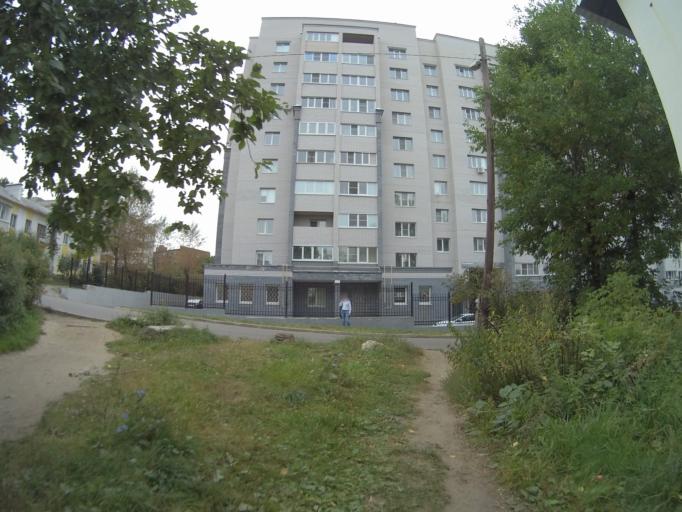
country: RU
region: Vladimir
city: Vladimir
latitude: 56.1263
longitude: 40.3578
